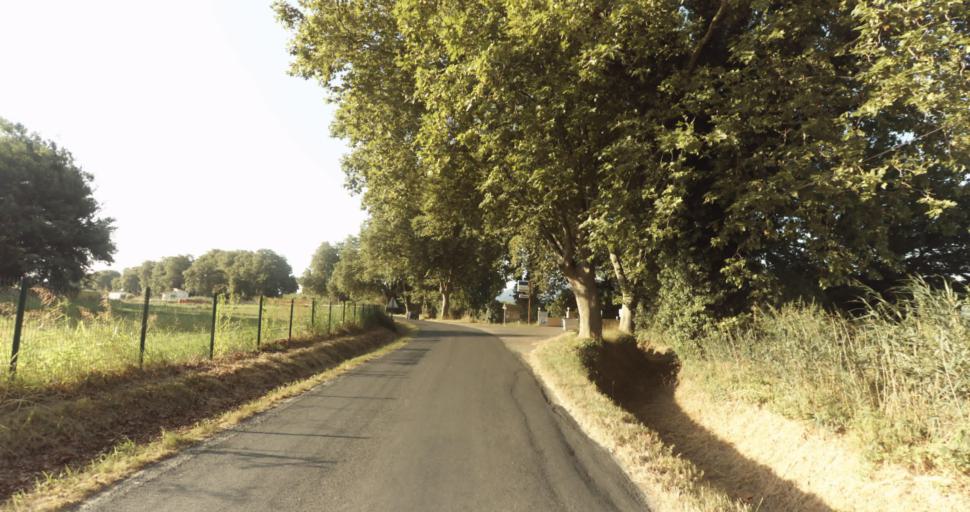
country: FR
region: Languedoc-Roussillon
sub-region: Departement des Pyrenees-Orientales
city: Latour-Bas-Elne
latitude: 42.6004
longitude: 3.0073
